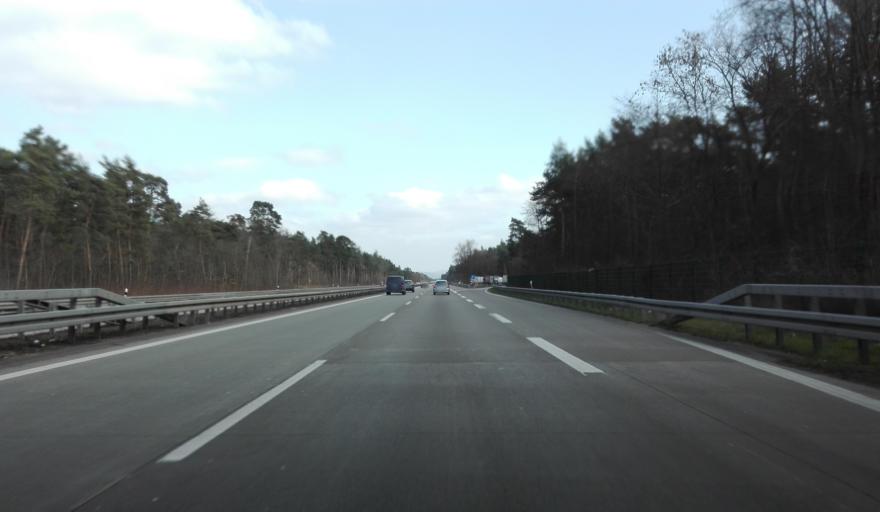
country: DE
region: Hesse
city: Lampertheim
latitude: 49.5548
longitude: 8.5057
